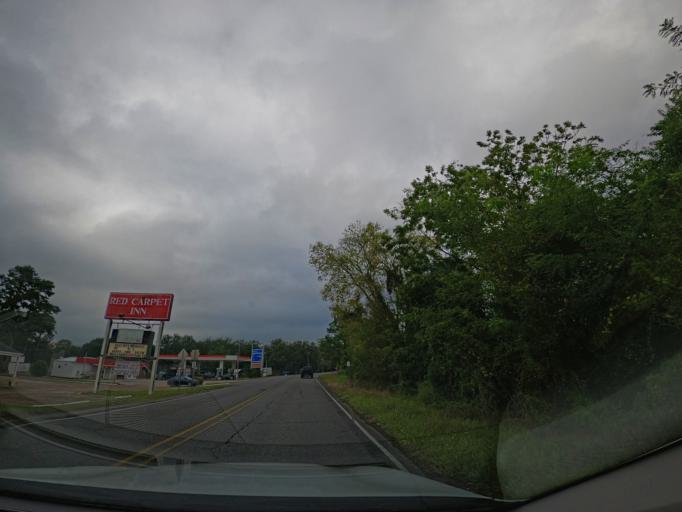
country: US
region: Louisiana
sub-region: Terrebonne Parish
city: Houma
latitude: 29.5742
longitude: -90.7476
